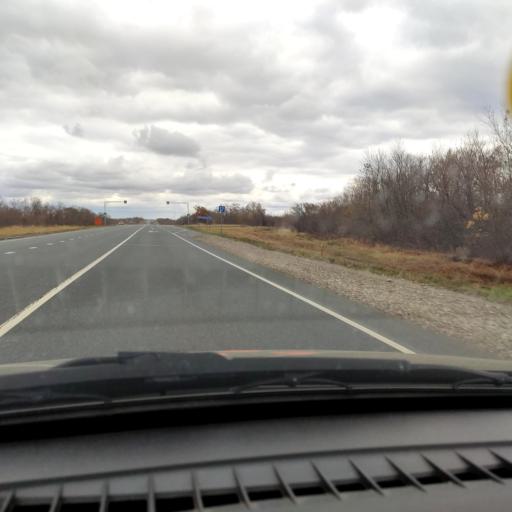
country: RU
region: Samara
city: Mezhdurechensk
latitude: 53.2583
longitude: 49.1006
